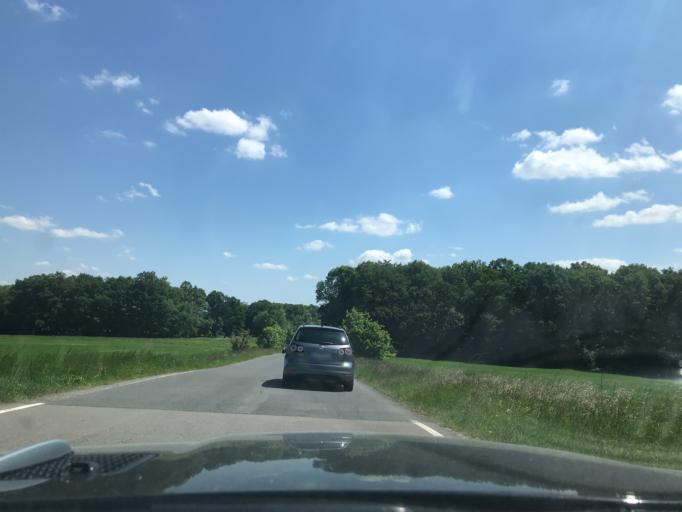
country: DE
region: Thuringia
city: Plaue
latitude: 50.7421
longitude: 10.9407
